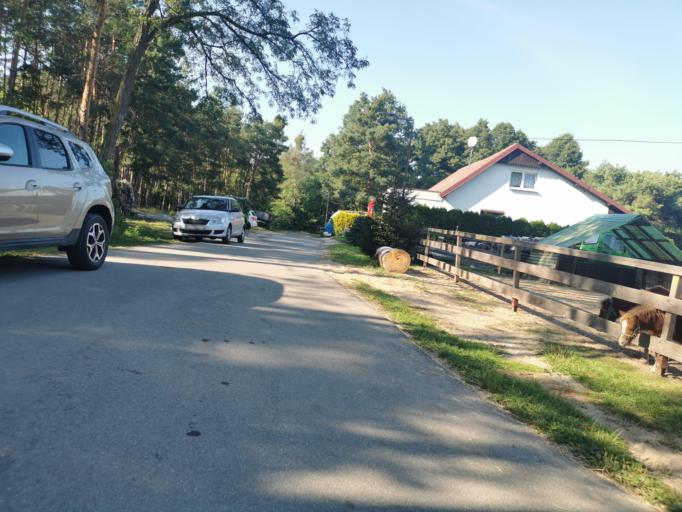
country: SK
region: Trnavsky
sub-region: Okres Senica
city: Senica
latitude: 48.6459
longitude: 17.2687
